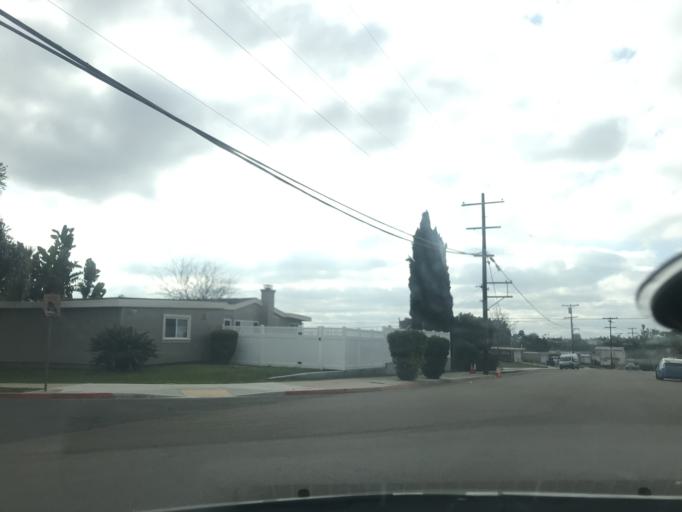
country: US
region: California
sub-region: San Diego County
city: San Diego
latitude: 32.7959
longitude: -117.1258
